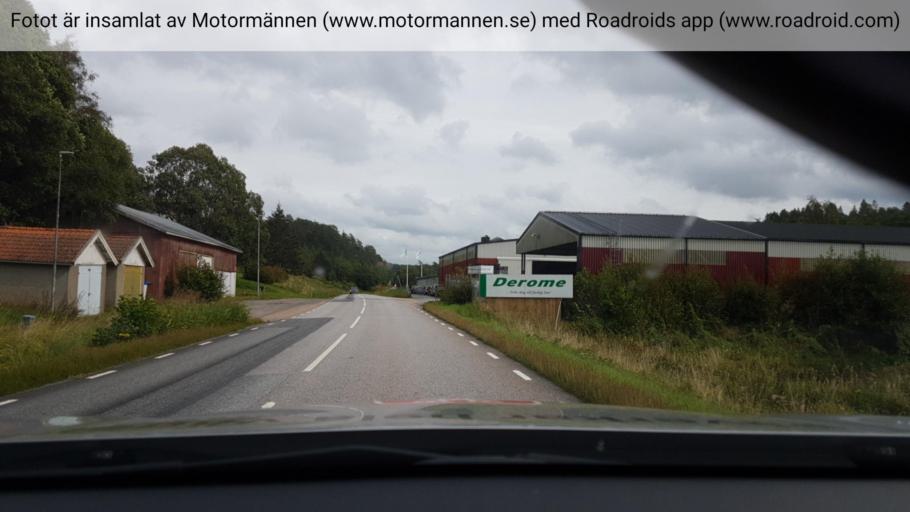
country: SE
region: Vaestra Goetaland
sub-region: Sotenas Kommun
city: Hunnebostrand
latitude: 58.5651
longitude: 11.3802
